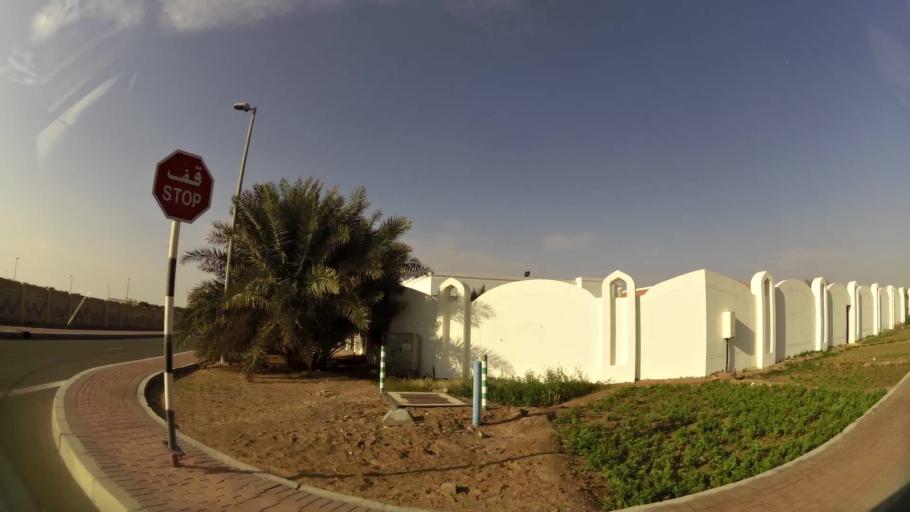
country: AE
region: Abu Dhabi
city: Al Ain
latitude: 24.0763
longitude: 55.8420
